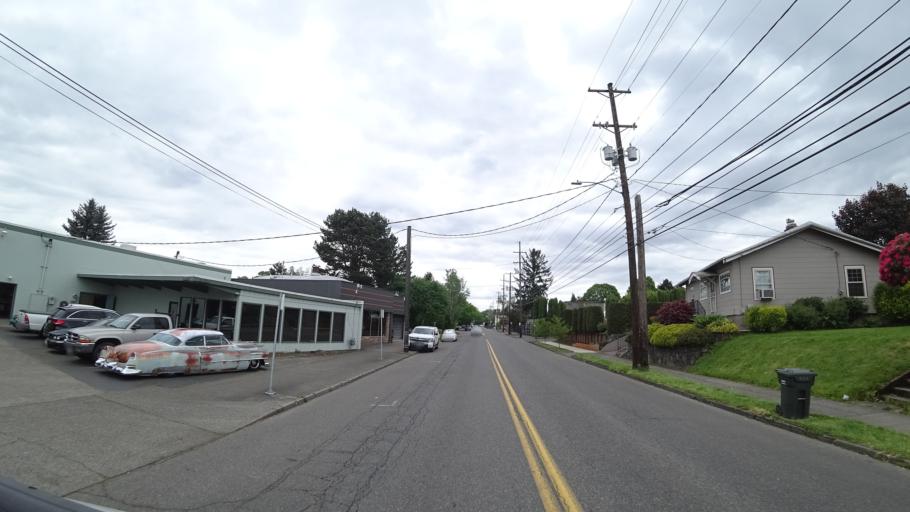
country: US
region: Oregon
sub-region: Multnomah County
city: Portland
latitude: 45.4935
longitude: -122.6526
